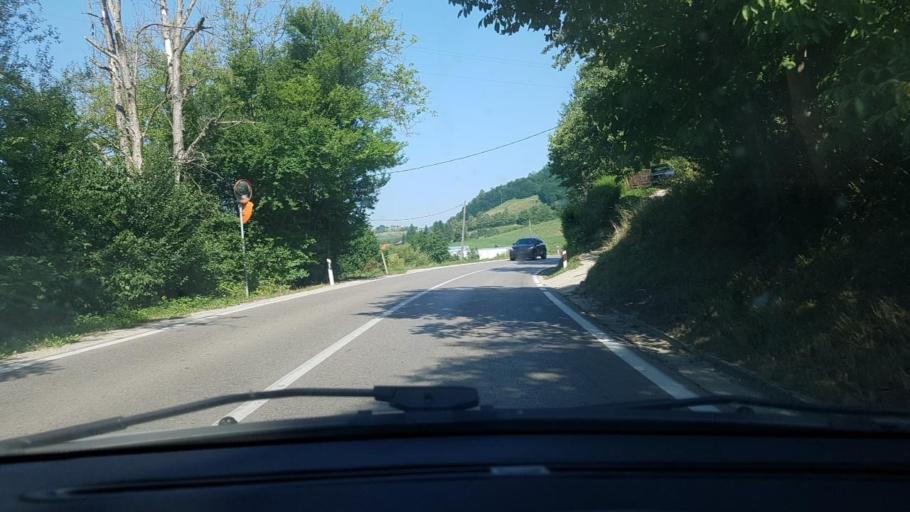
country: BA
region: Federation of Bosnia and Herzegovina
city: Sumatac
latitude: 45.1026
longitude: 15.8777
